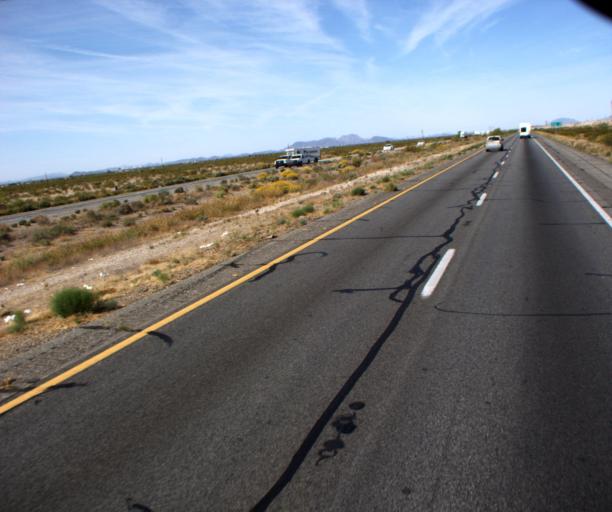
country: US
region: Arizona
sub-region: Maricopa County
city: Buckeye
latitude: 33.4423
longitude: -112.6902
